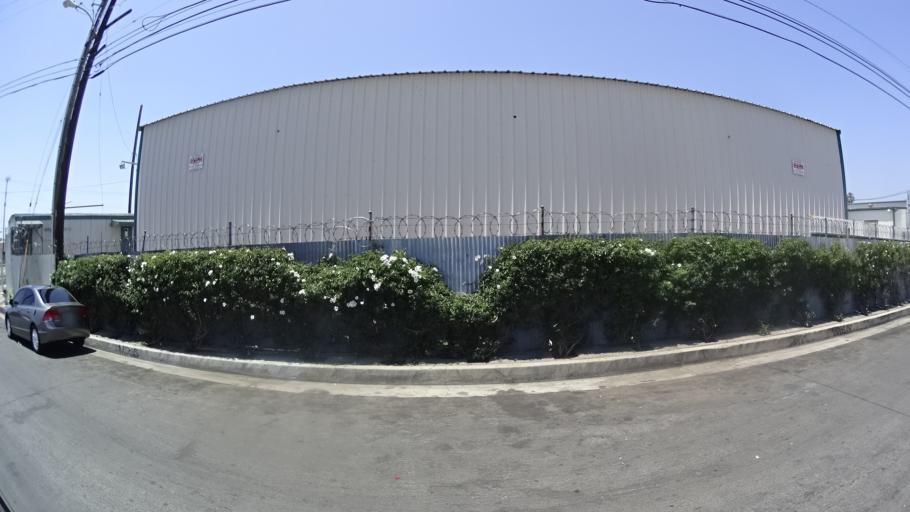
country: US
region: California
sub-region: Los Angeles County
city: Van Nuys
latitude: 34.2136
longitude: -118.4553
